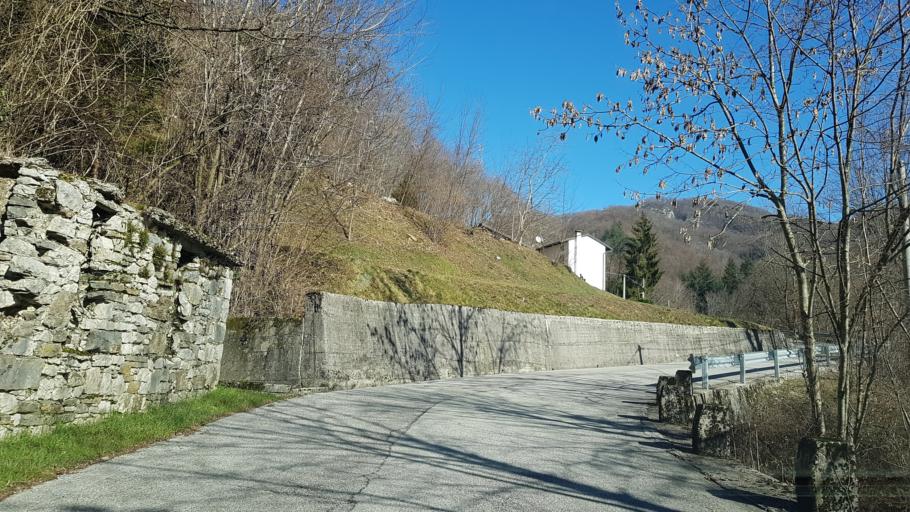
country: IT
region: Friuli Venezia Giulia
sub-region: Provincia di Udine
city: Nimis
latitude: 46.2261
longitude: 13.2996
